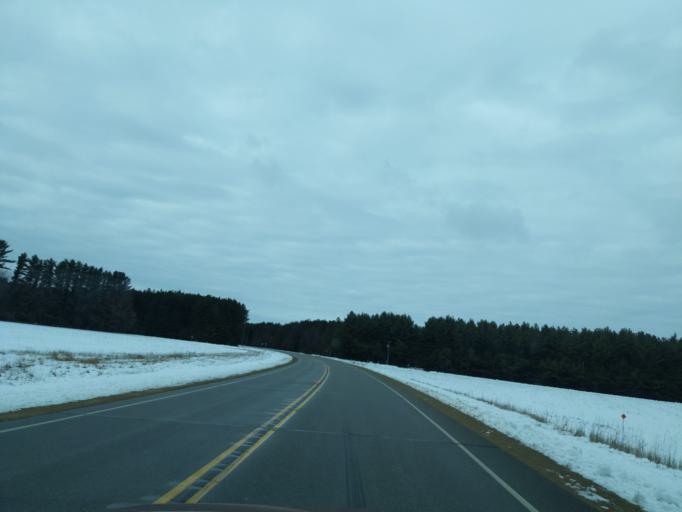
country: US
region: Wisconsin
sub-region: Waushara County
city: Wautoma
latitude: 43.9579
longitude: -89.3182
